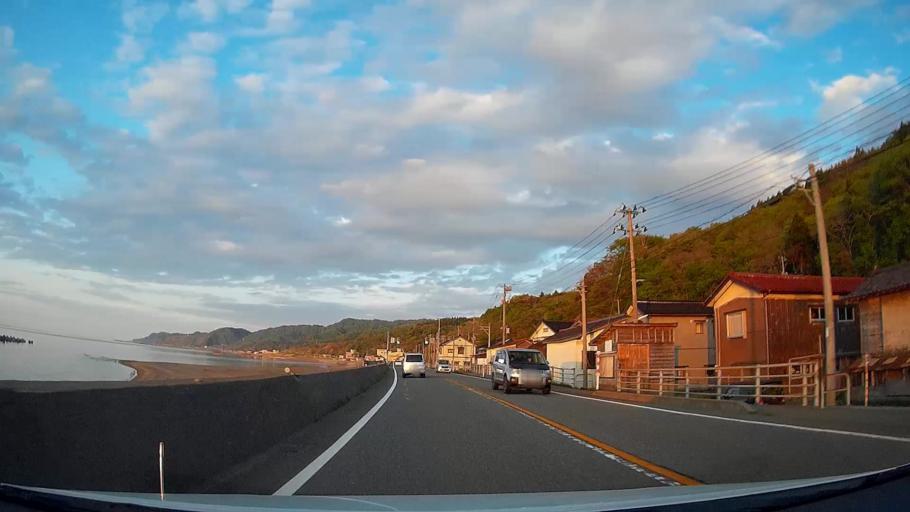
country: JP
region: Niigata
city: Itoigawa
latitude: 37.1141
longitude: 138.0188
